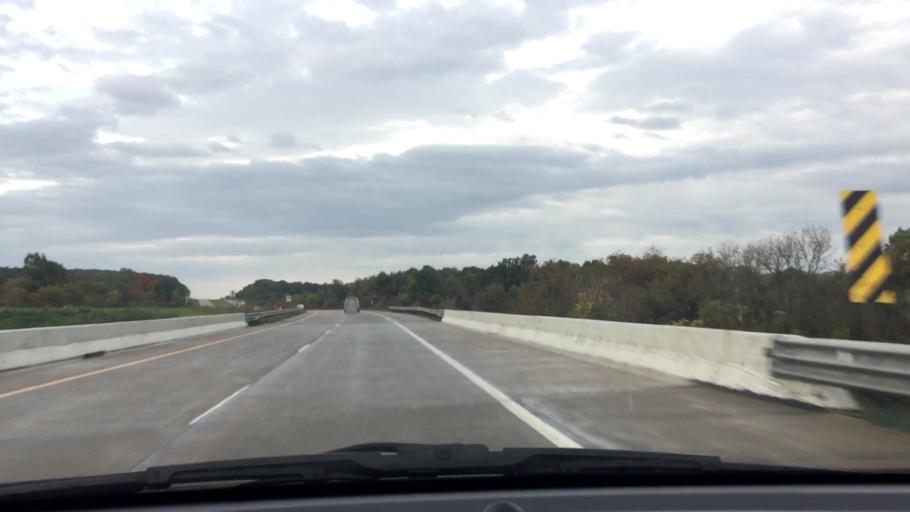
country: US
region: Wisconsin
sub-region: Rock County
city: Clinton
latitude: 42.5702
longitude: -88.9008
